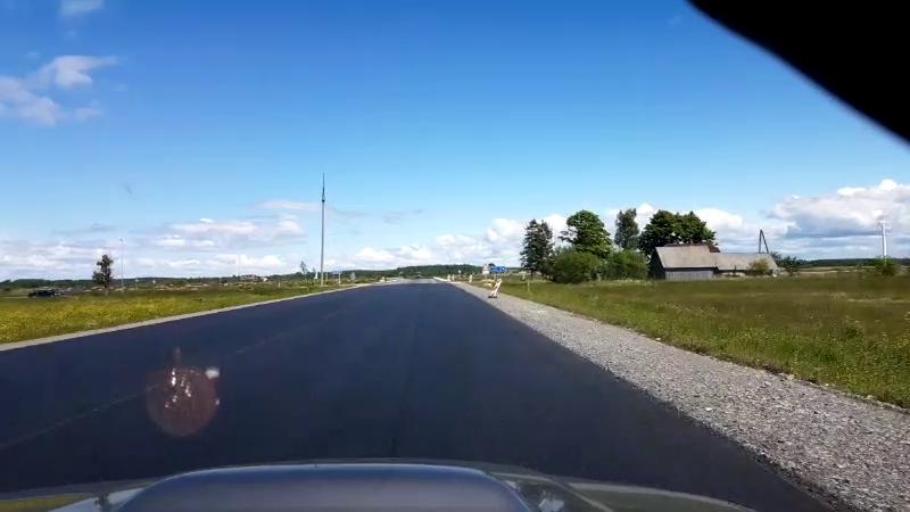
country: LV
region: Salacgrivas
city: Ainazi
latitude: 57.8629
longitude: 24.3699
